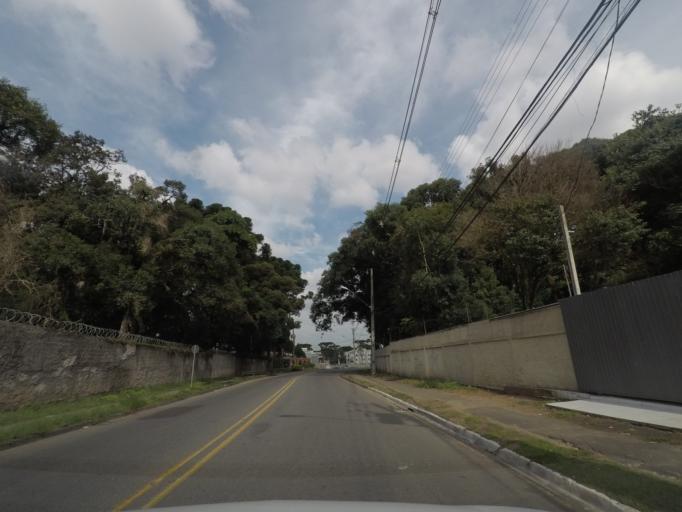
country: BR
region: Parana
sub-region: Pinhais
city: Pinhais
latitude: -25.4845
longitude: -49.2132
